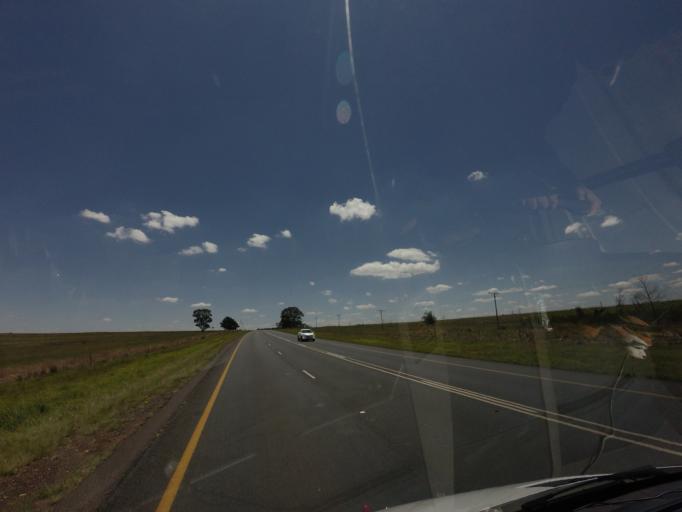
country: ZA
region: Mpumalanga
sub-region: Nkangala District Municipality
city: Belfast
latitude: -25.7335
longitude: 30.1210
